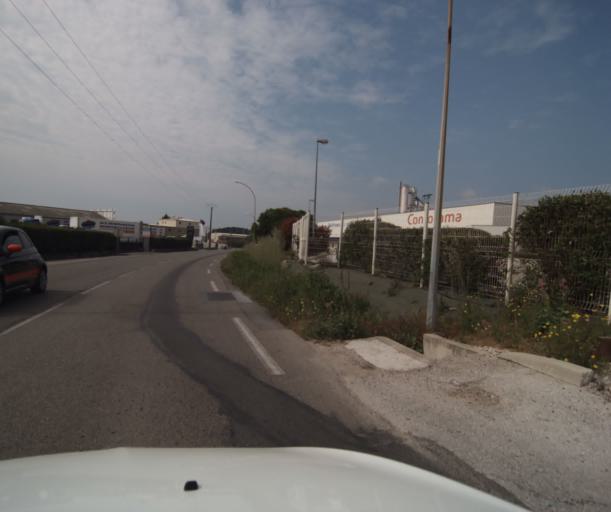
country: FR
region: Provence-Alpes-Cote d'Azur
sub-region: Departement du Var
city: La Farlede
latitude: 43.1474
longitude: 6.0357
